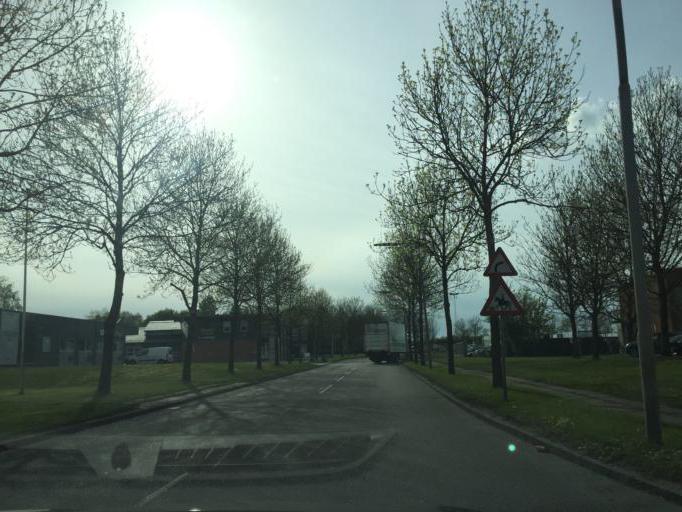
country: DK
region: South Denmark
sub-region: Odense Kommune
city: Bellinge
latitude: 55.3588
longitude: 10.3257
